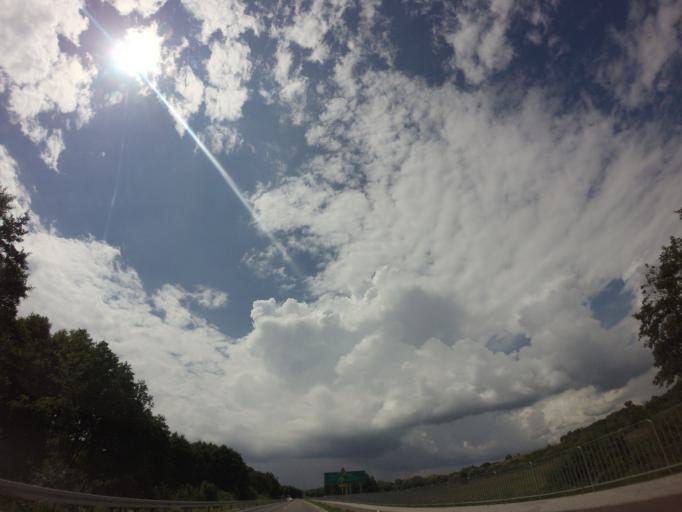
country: PL
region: Masovian Voivodeship
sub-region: Powiat lipski
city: Solec Nad Wisla
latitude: 51.1258
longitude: 21.7654
